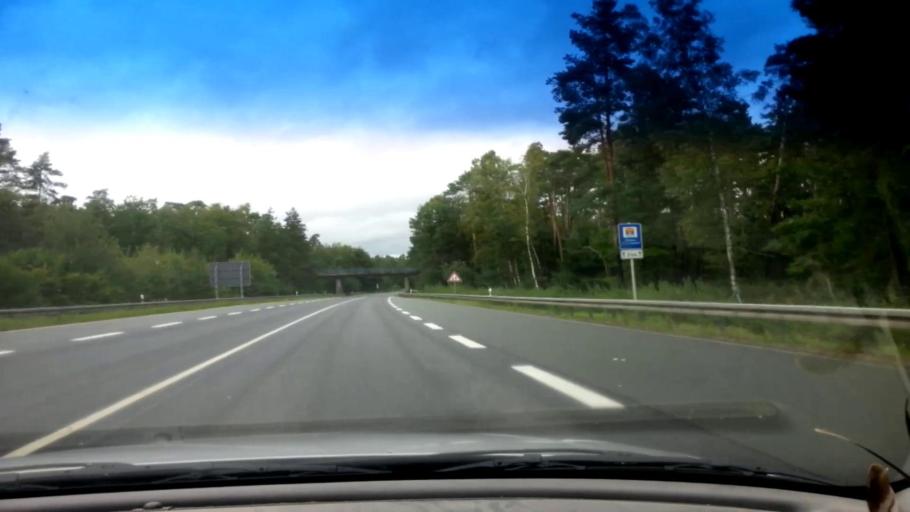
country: DE
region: Bavaria
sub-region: Upper Franconia
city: Strullendorf
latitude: 49.8672
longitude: 10.9467
